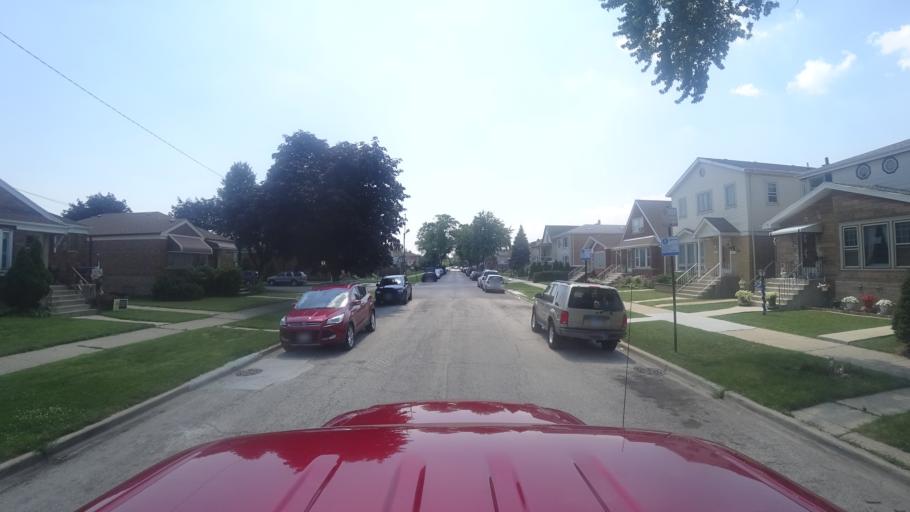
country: US
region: Illinois
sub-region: Cook County
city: Cicero
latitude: 41.7953
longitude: -87.7343
